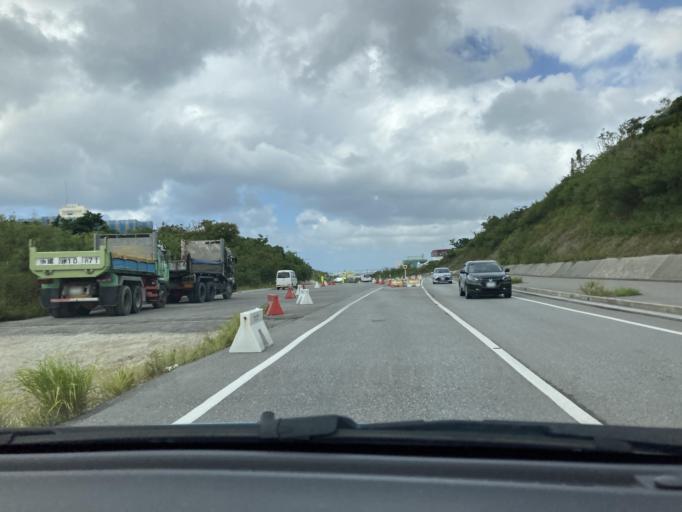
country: JP
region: Okinawa
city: Ginowan
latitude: 26.2660
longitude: 127.7091
